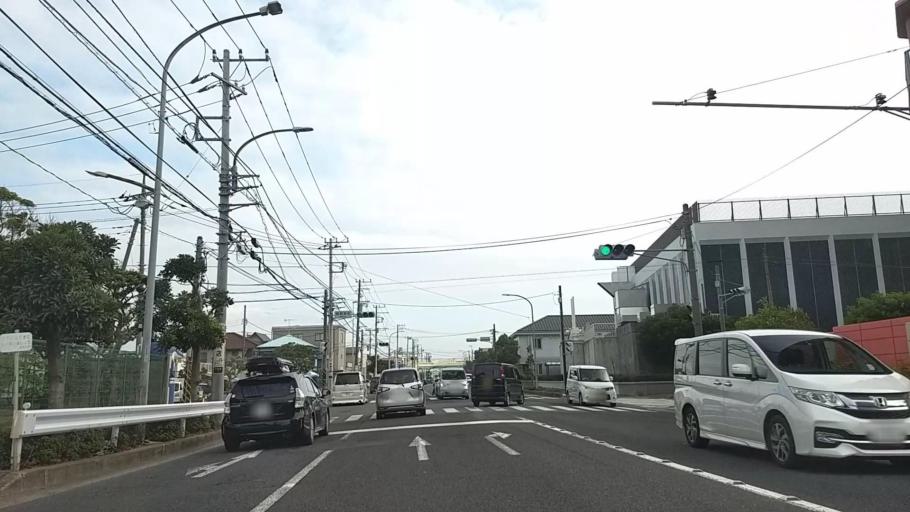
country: JP
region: Kanagawa
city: Hiratsuka
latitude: 35.3264
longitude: 139.3603
